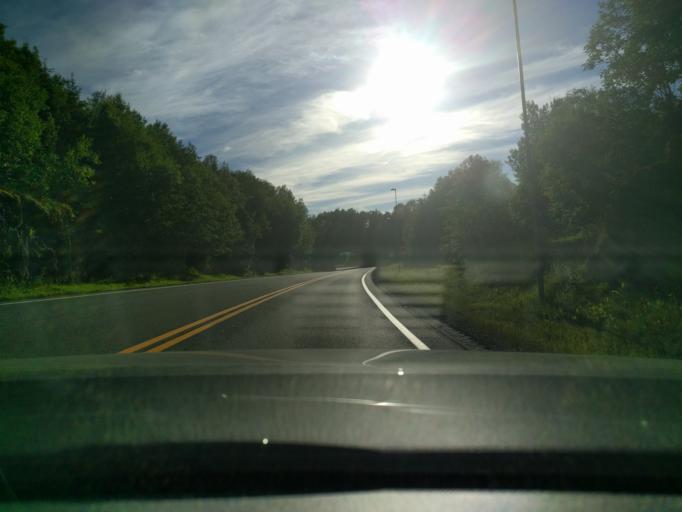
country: NO
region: Vestfold
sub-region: Holmestrand
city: Gullhaug
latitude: 59.5071
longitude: 10.2015
